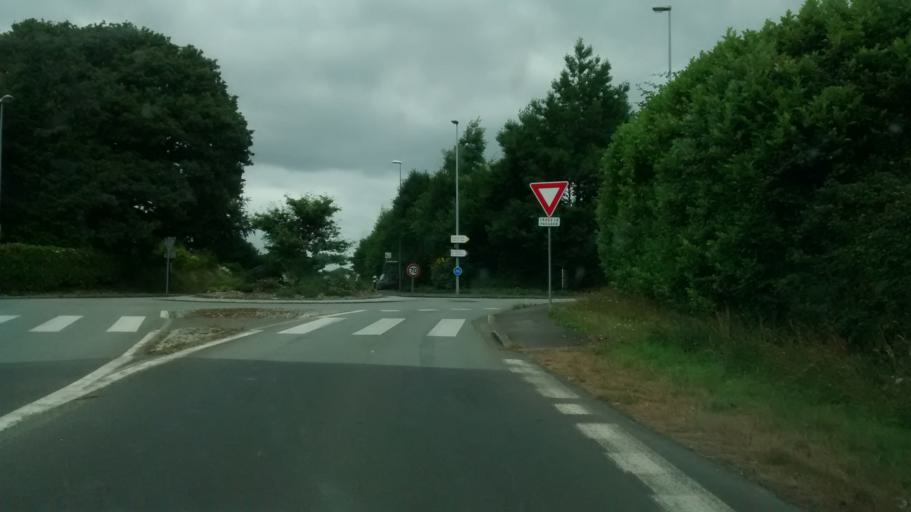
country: FR
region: Brittany
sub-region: Departement du Finistere
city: Plougastel-Daoulas
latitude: 48.3719
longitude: -4.3796
